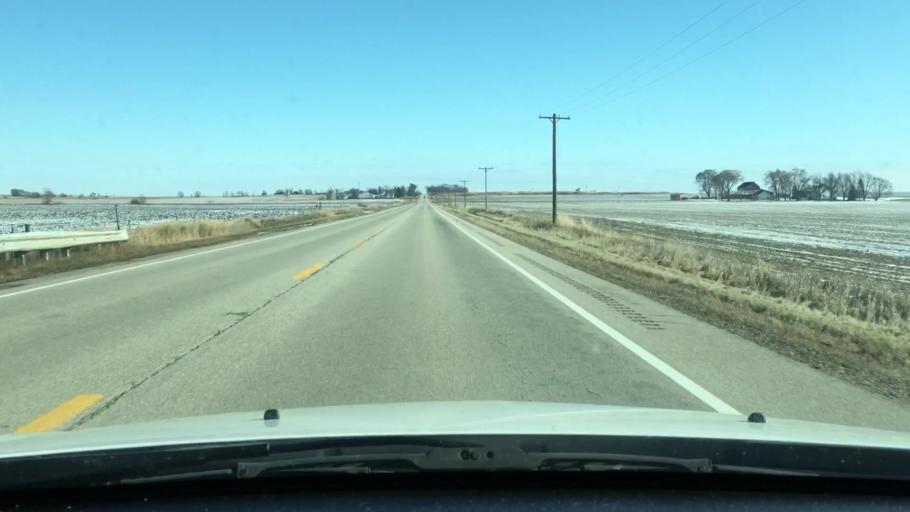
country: US
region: Illinois
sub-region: DeKalb County
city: Malta
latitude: 42.0008
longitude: -88.9236
